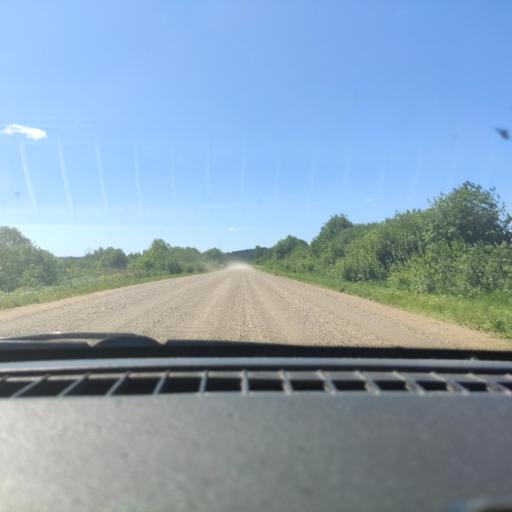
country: RU
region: Perm
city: Verkhnechusovskiye Gorodki
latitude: 58.1953
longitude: 57.1366
